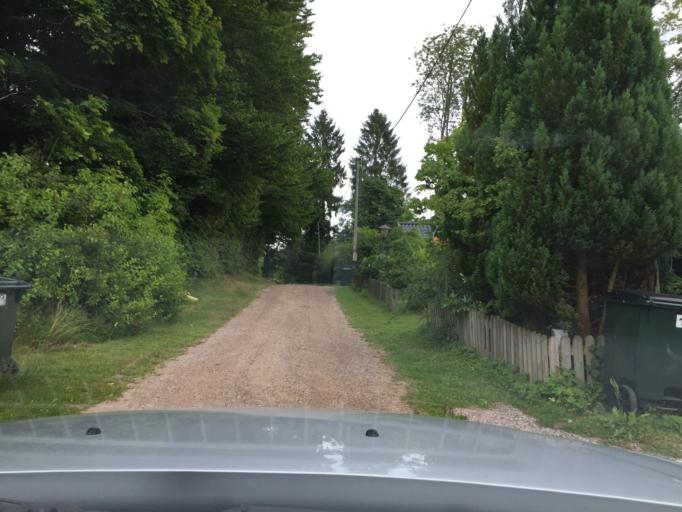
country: SE
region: Skane
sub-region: Hassleholms Kommun
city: Sosdala
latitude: 56.0062
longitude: 13.6365
